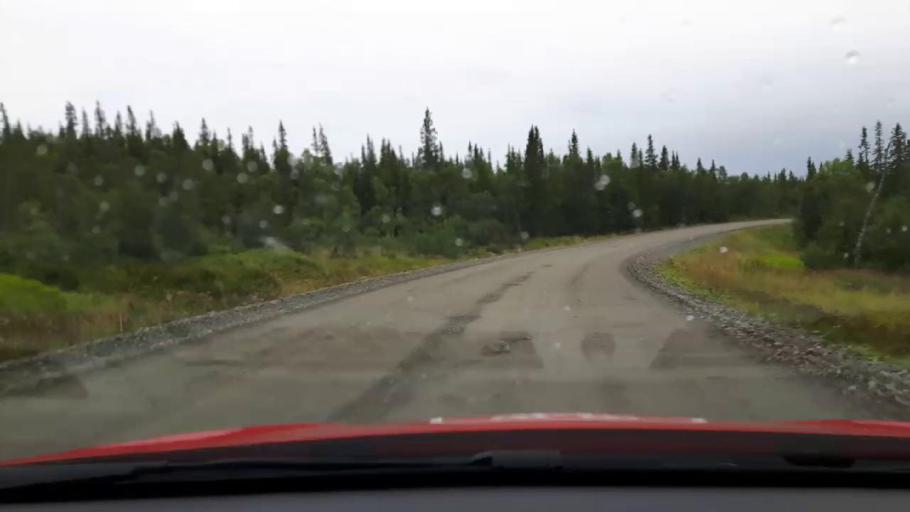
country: NO
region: Nord-Trondelag
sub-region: Meraker
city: Meraker
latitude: 63.5555
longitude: 12.3707
